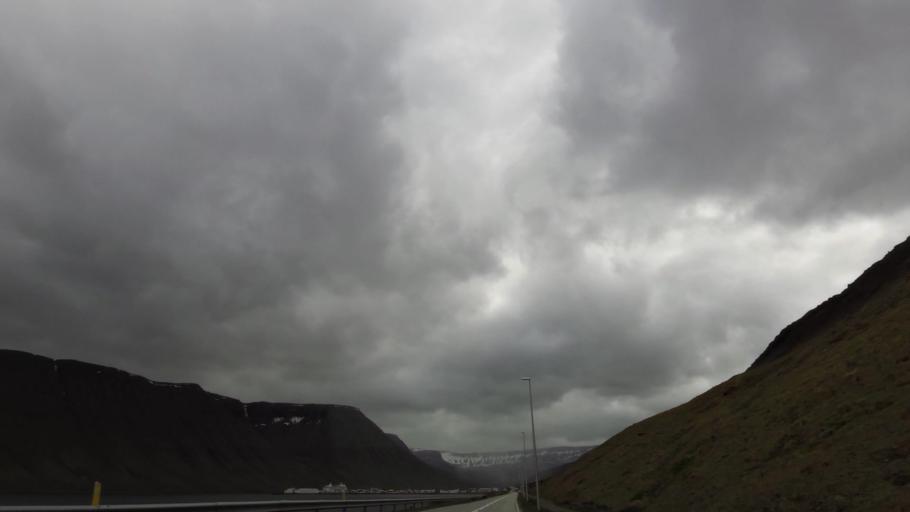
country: IS
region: Westfjords
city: Isafjoerdur
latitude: 66.0917
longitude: -23.1142
